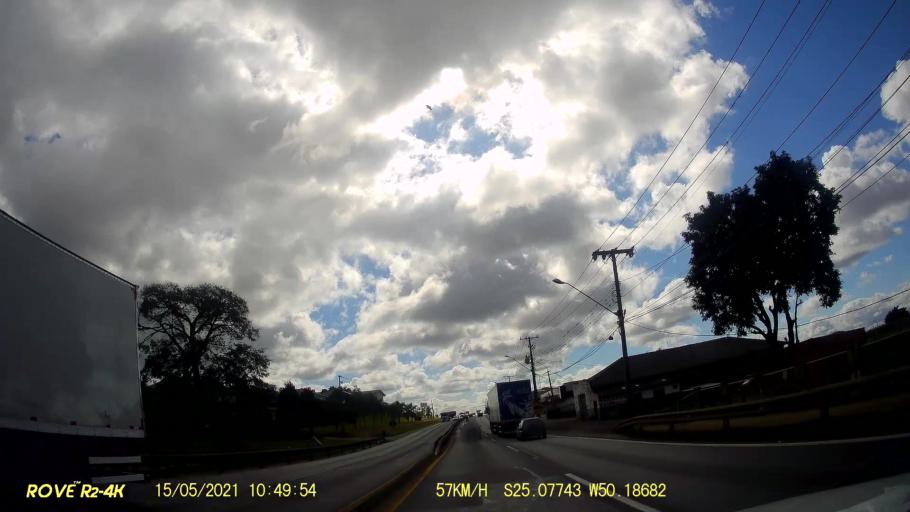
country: BR
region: Parana
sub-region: Ponta Grossa
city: Ponta Grossa
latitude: -25.0773
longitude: -50.1868
